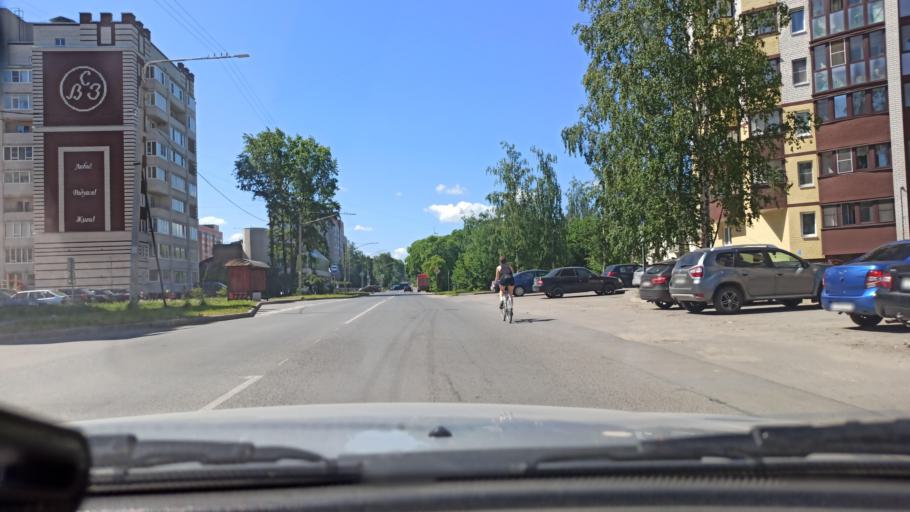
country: RU
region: Vologda
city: Vologda
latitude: 59.2168
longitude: 39.8489
